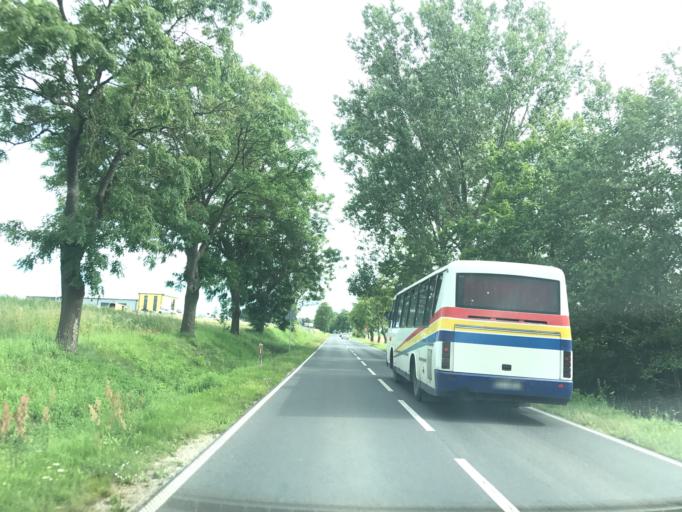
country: PL
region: Kujawsko-Pomorskie
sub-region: Powiat rypinski
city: Rypin
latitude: 53.1028
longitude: 19.3934
